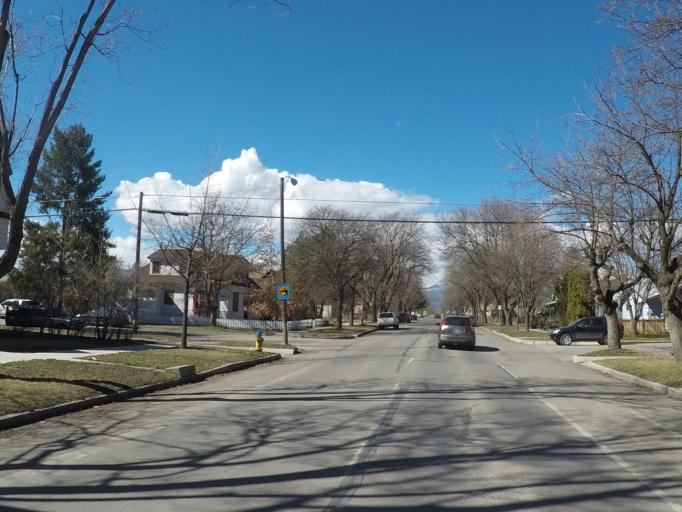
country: US
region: Montana
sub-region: Missoula County
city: Missoula
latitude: 46.8650
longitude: -114.0061
